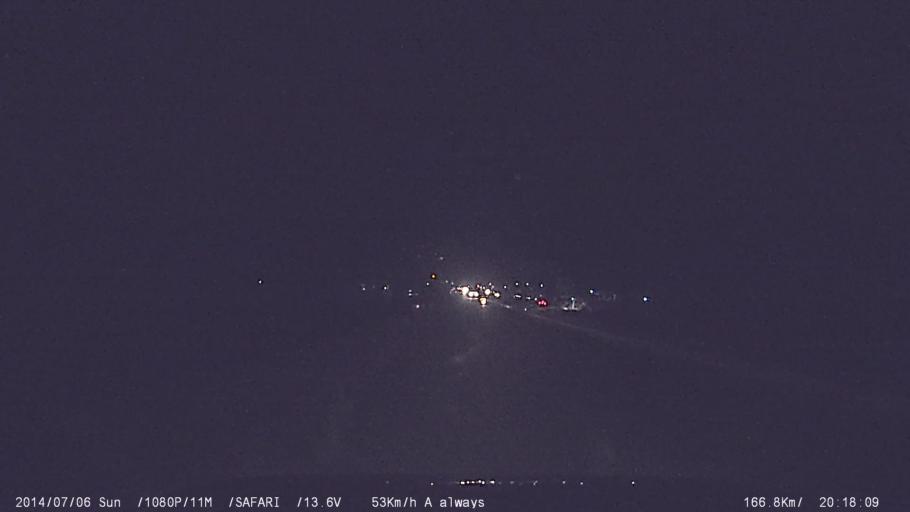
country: IN
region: Kerala
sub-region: Palakkad district
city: Palakkad
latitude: 10.7753
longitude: 76.7019
